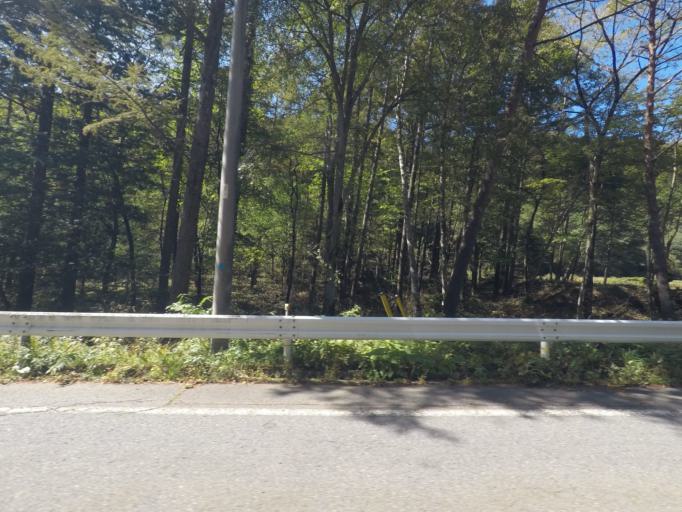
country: JP
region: Nagano
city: Shiojiri
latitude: 35.9969
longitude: 137.7387
